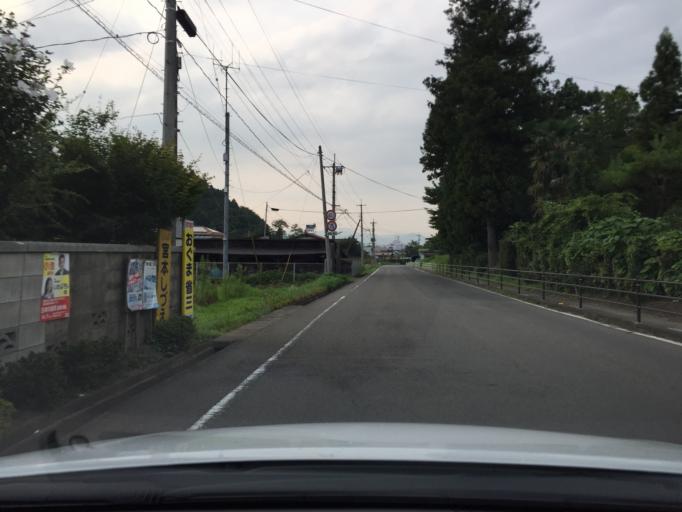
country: JP
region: Fukushima
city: Fukushima-shi
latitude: 37.7196
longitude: 140.4735
